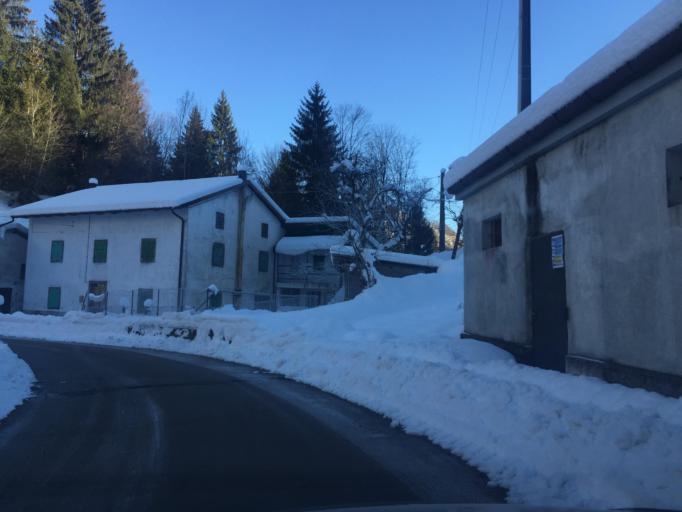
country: IT
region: Friuli Venezia Giulia
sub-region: Provincia di Udine
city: Lauco
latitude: 46.4396
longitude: 12.9460
